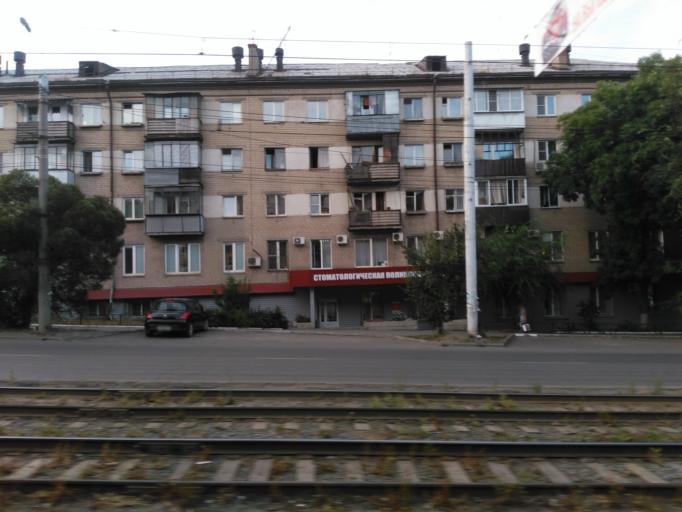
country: RU
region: Chelyabinsk
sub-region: Gorod Chelyabinsk
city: Chelyabinsk
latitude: 55.1841
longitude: 61.3927
